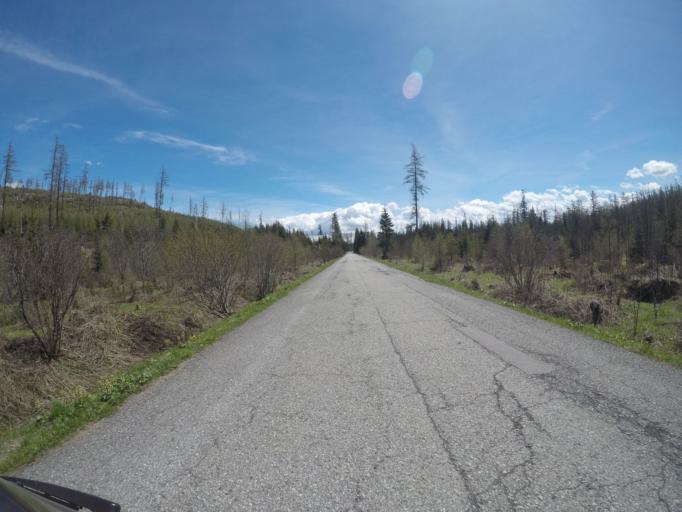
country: SK
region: Presovsky
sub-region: Okres Poprad
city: Strba
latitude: 49.1189
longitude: 20.0771
